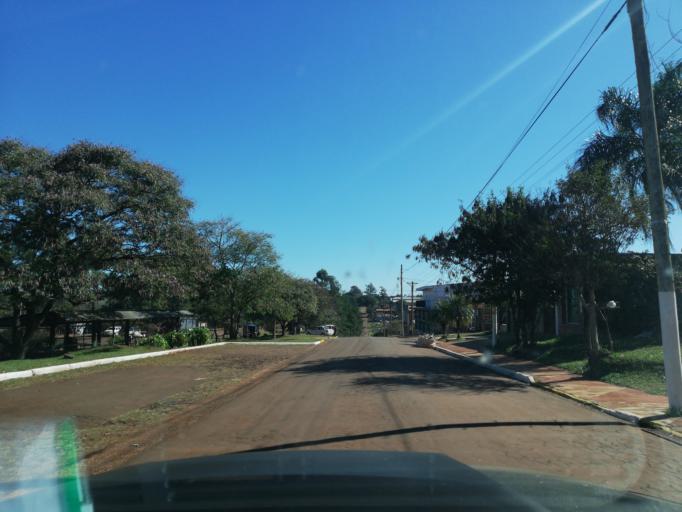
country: AR
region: Misiones
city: Aristobulo del Valle
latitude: -27.0846
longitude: -54.8316
